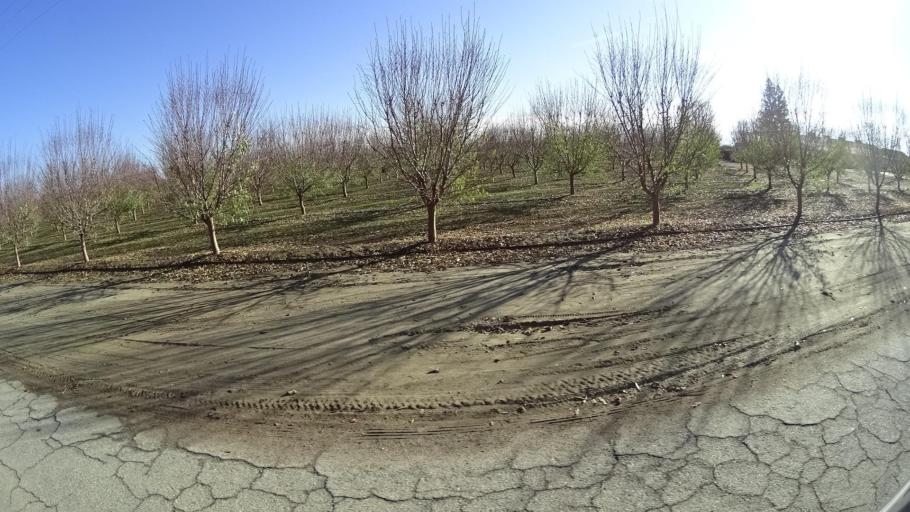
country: US
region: California
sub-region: Kern County
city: McFarland
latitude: 35.6908
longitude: -119.2942
